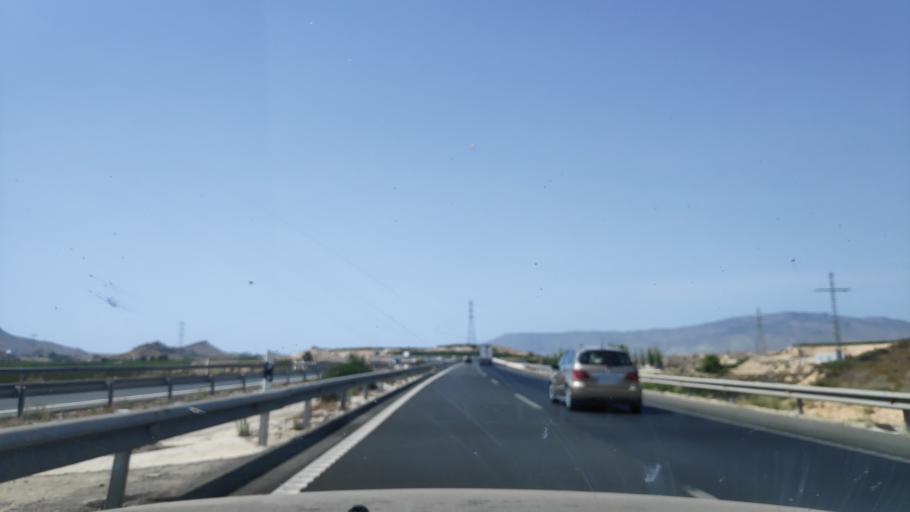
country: ES
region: Murcia
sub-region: Murcia
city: Archena
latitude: 38.1406
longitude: -1.2732
